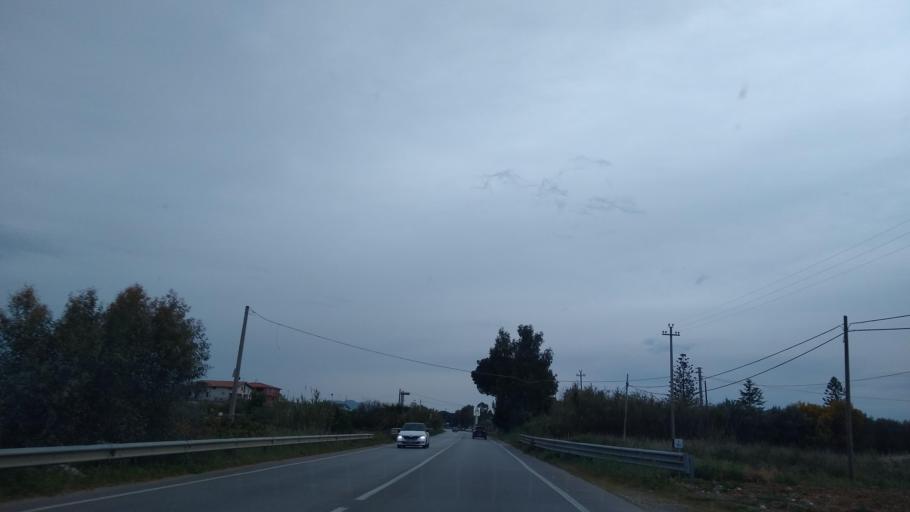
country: IT
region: Sicily
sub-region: Palermo
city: Partinico
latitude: 38.0324
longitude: 13.0965
